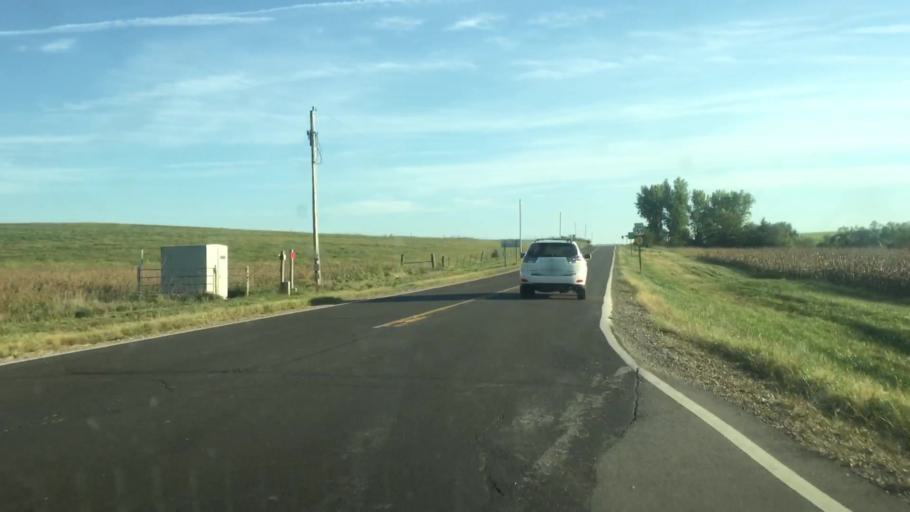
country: US
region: Kansas
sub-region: Brown County
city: Horton
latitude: 39.5862
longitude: -95.5270
